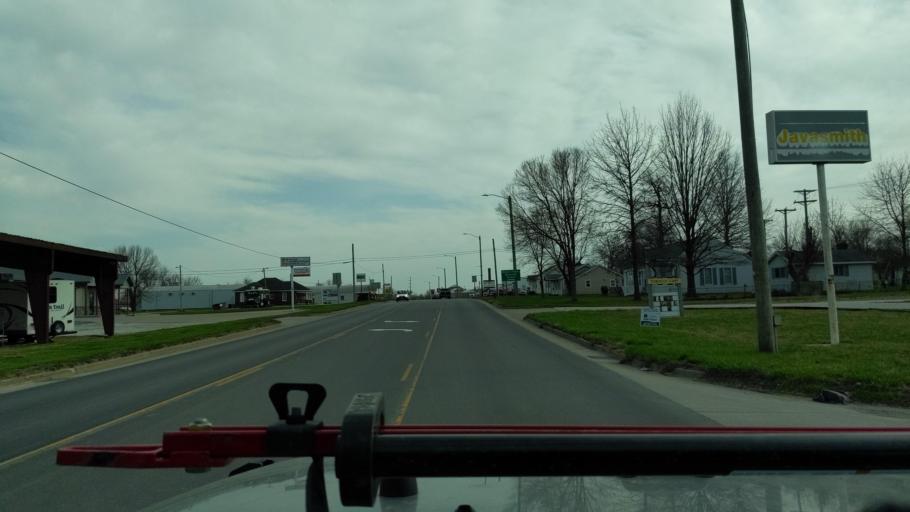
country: US
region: Missouri
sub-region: Macon County
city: Macon
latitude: 39.7277
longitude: -92.4660
